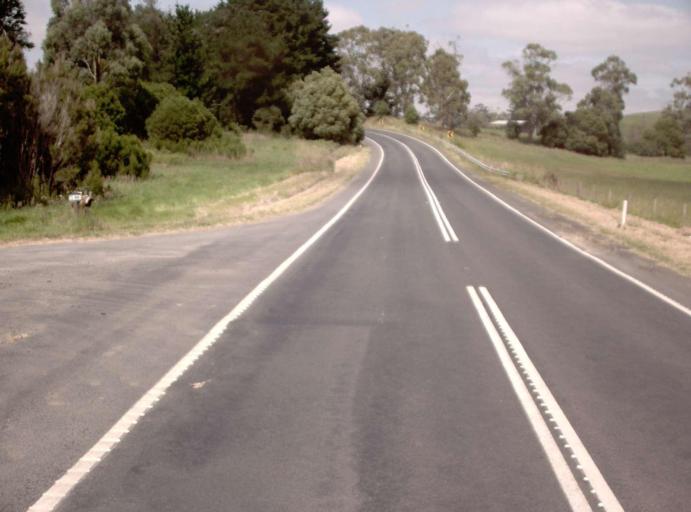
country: AU
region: Victoria
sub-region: Baw Baw
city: Warragul
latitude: -38.4316
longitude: 146.0360
